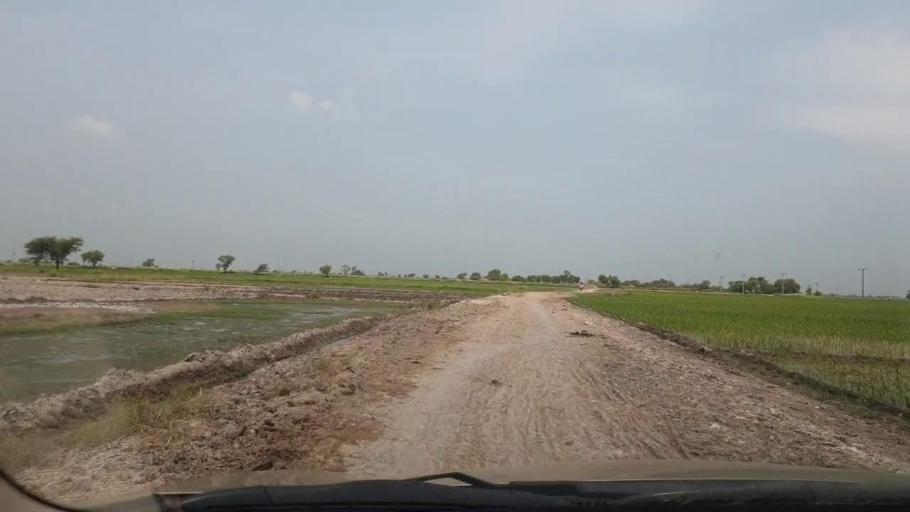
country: PK
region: Sindh
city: Goth Garelo
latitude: 27.5186
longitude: 68.1228
